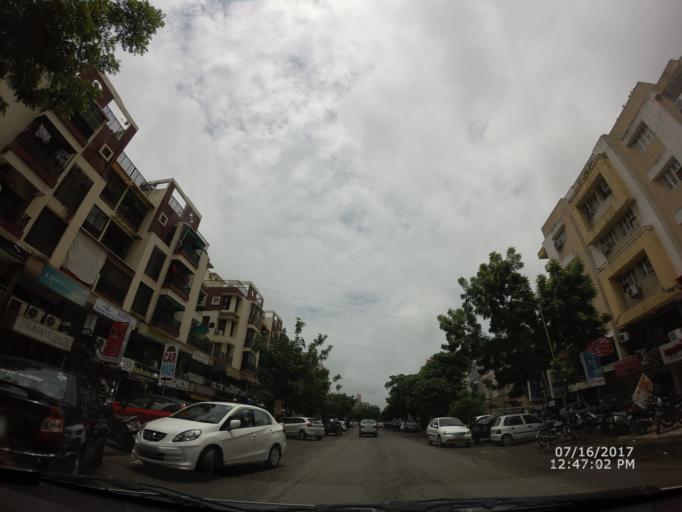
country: IN
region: Gujarat
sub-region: Ahmadabad
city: Sarkhej
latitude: 23.0187
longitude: 72.5150
